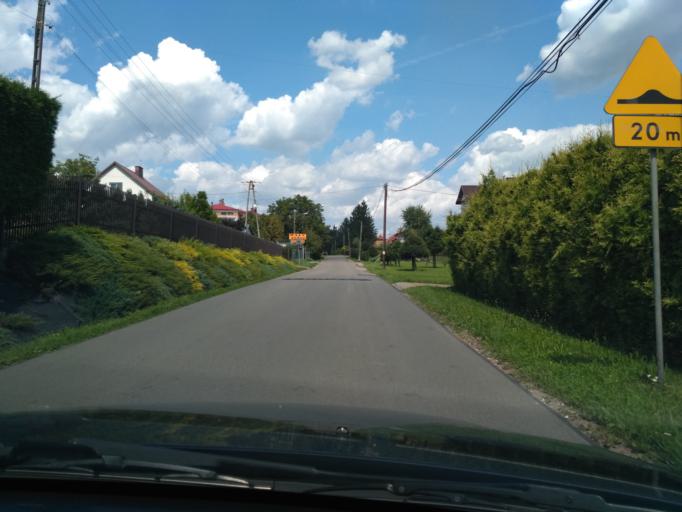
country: PL
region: Subcarpathian Voivodeship
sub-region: Powiat strzyzowski
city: Strzyzow
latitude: 49.8776
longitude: 21.7556
